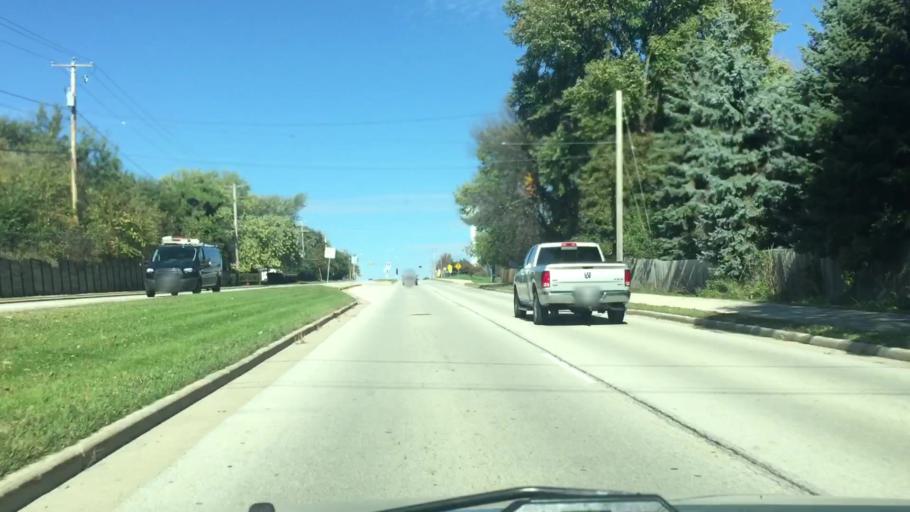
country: US
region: Wisconsin
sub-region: Waukesha County
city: Waukesha
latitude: 43.0276
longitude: -88.1668
